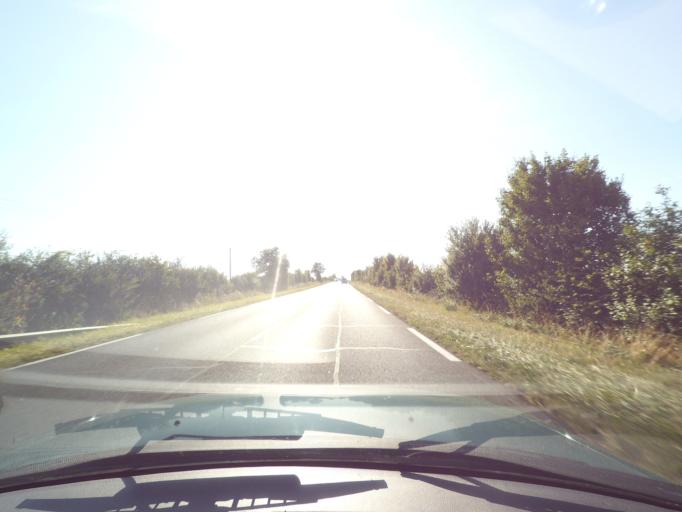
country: FR
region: Poitou-Charentes
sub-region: Departement de la Vienne
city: Ayron
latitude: 46.6569
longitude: 0.0973
